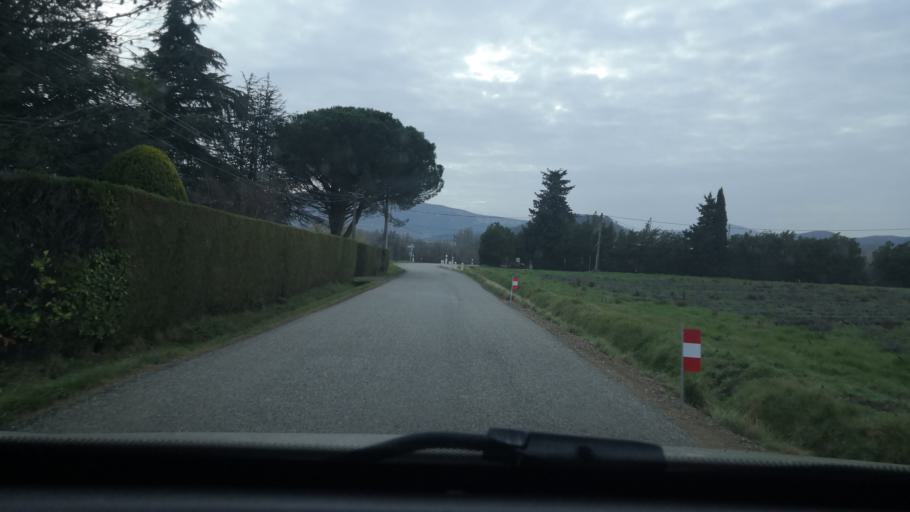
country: FR
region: Rhone-Alpes
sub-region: Departement de la Drome
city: La Begude-de-Mazenc
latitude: 44.5631
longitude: 4.9184
